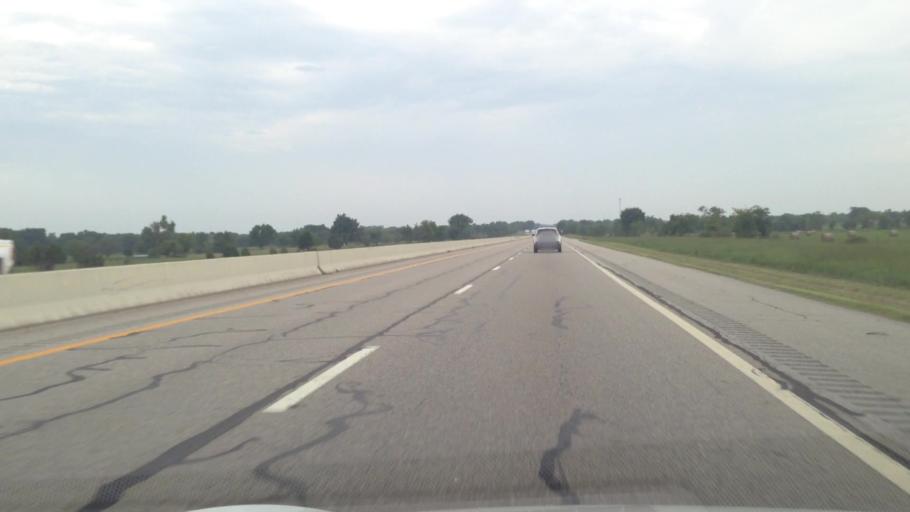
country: US
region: Oklahoma
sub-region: Ottawa County
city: Fairland
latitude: 36.7938
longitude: -94.8838
